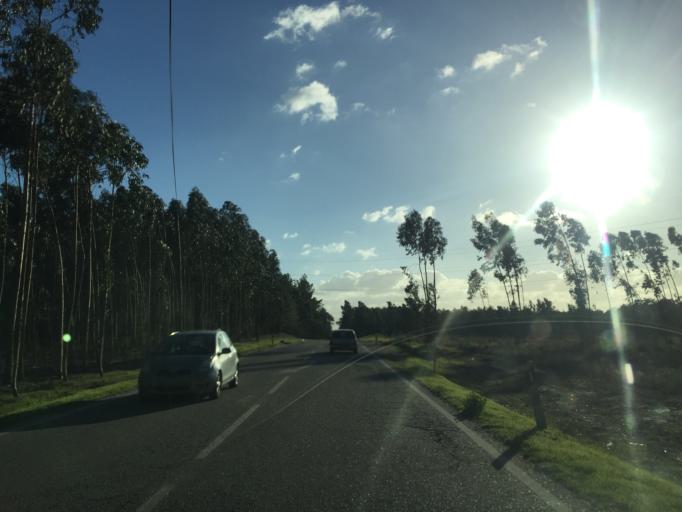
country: PT
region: Leiria
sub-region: Leiria
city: Monte Redondo
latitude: 39.9301
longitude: -8.8032
